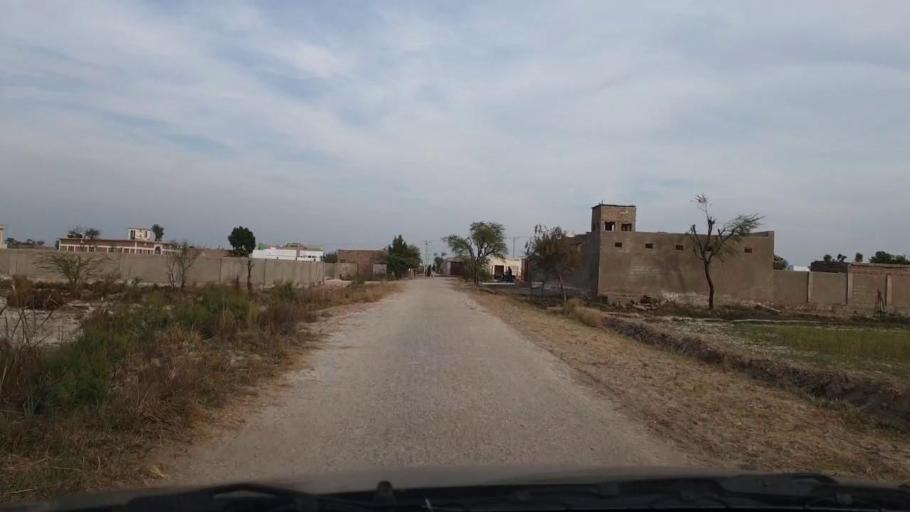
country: PK
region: Sindh
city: Khadro
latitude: 26.1879
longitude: 68.7333
